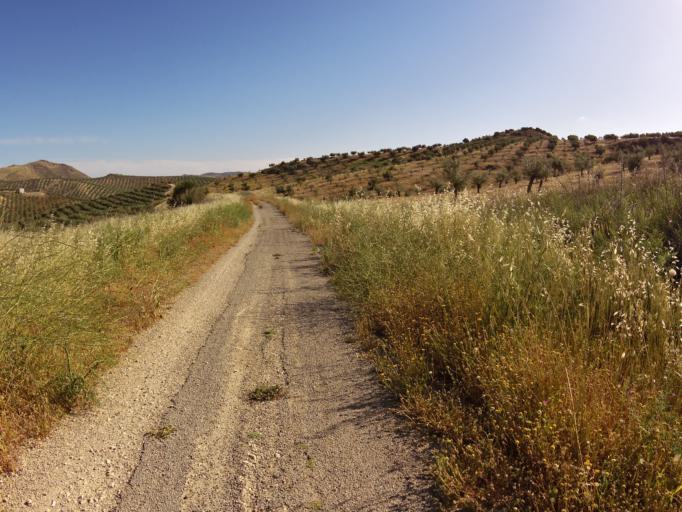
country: ES
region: Andalusia
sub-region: Province of Cordoba
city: Fuente-Tojar
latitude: 37.5811
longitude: -4.1772
